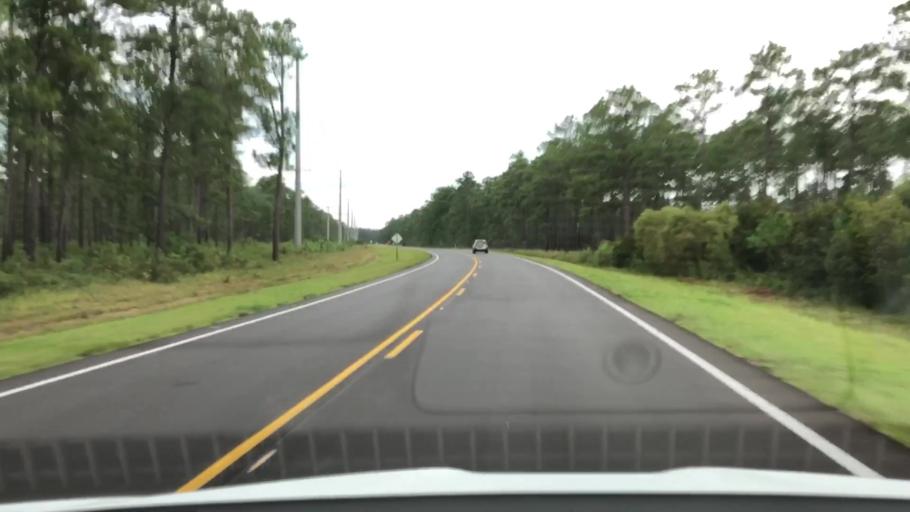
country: US
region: North Carolina
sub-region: Onslow County
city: Swansboro
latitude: 34.8092
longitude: -77.1353
